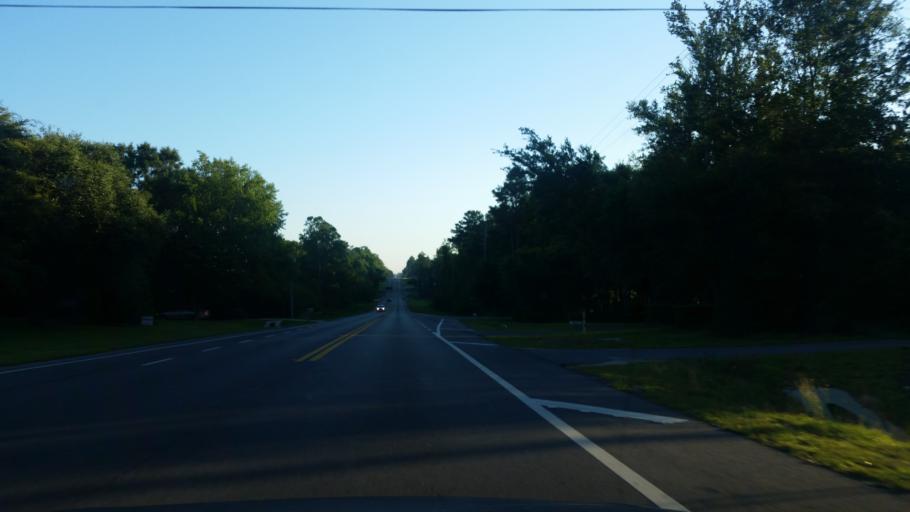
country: US
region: Florida
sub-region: Escambia County
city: Gonzalez
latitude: 30.5599
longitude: -87.3289
